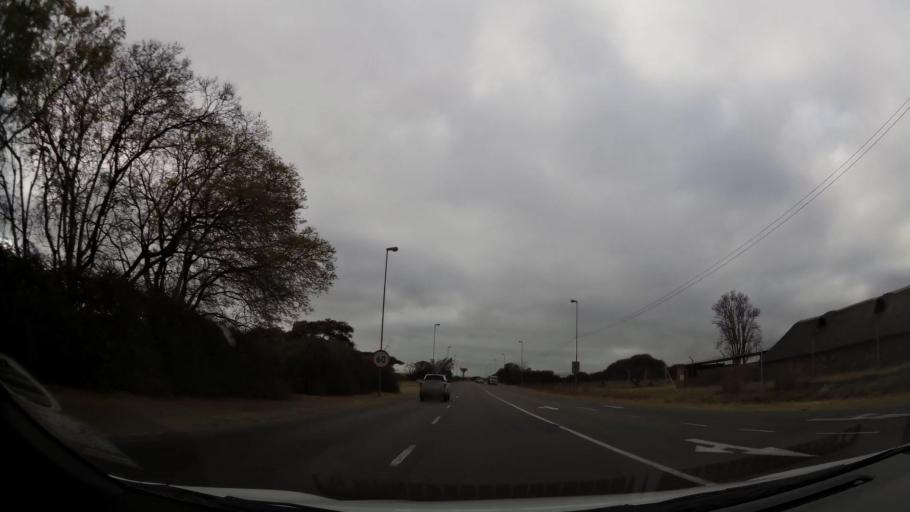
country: ZA
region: Limpopo
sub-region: Capricorn District Municipality
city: Polokwane
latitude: -23.8726
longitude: 29.4557
